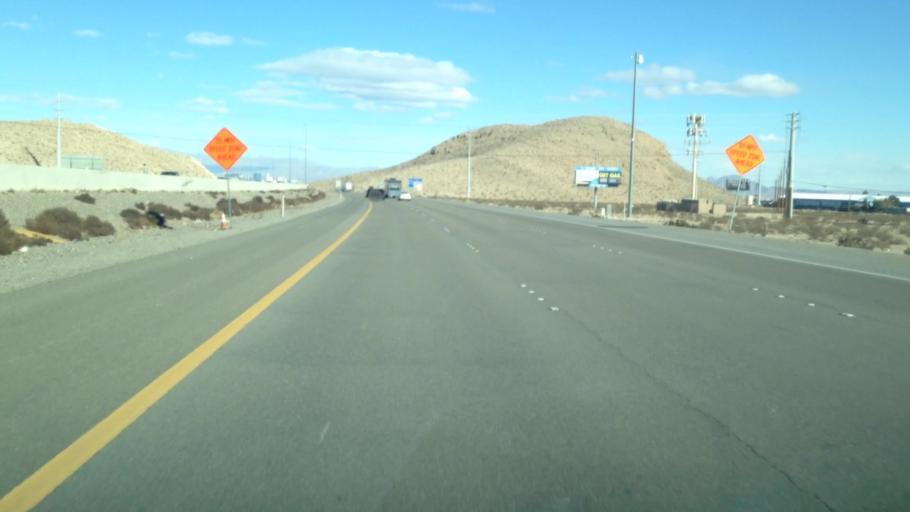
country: US
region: Nevada
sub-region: Clark County
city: Enterprise
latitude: 35.9465
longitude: -115.1831
